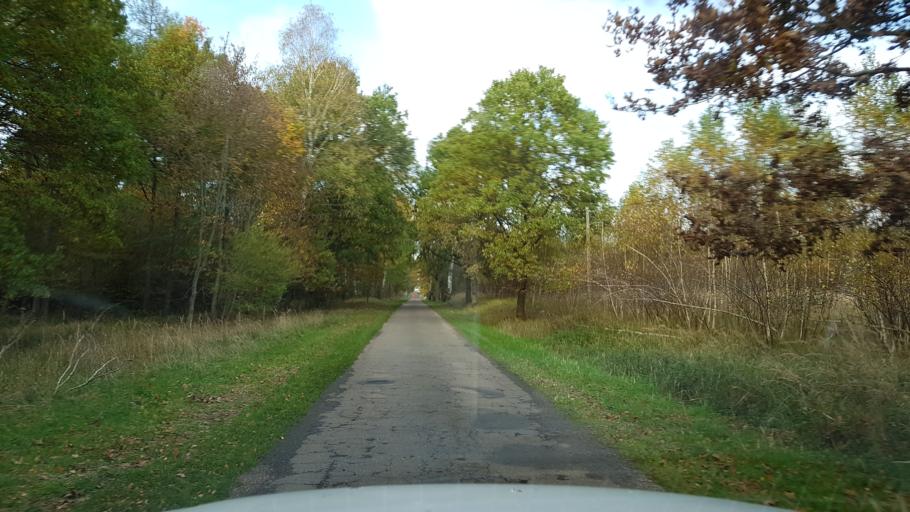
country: PL
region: West Pomeranian Voivodeship
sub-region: Powiat lobeski
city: Wegorzyno
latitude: 53.5121
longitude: 15.4962
